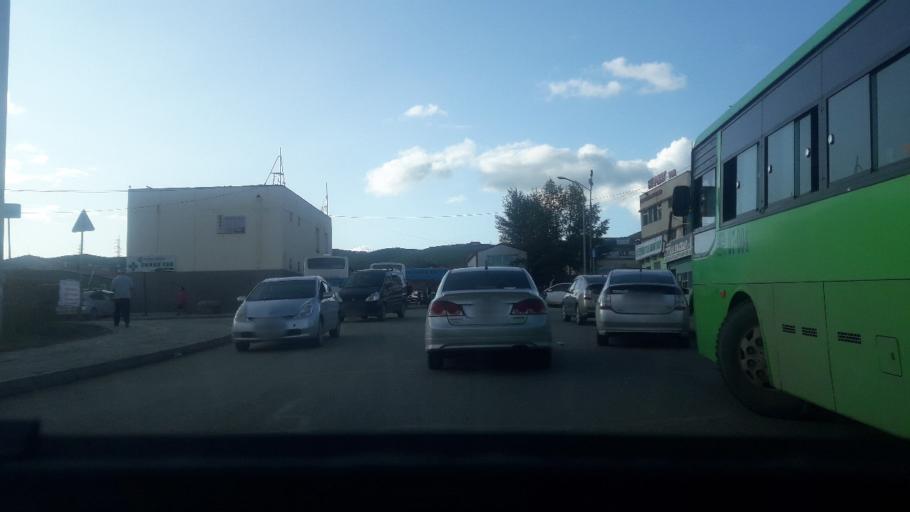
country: MN
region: Ulaanbaatar
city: Ulaanbaatar
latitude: 47.9343
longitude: 107.0063
